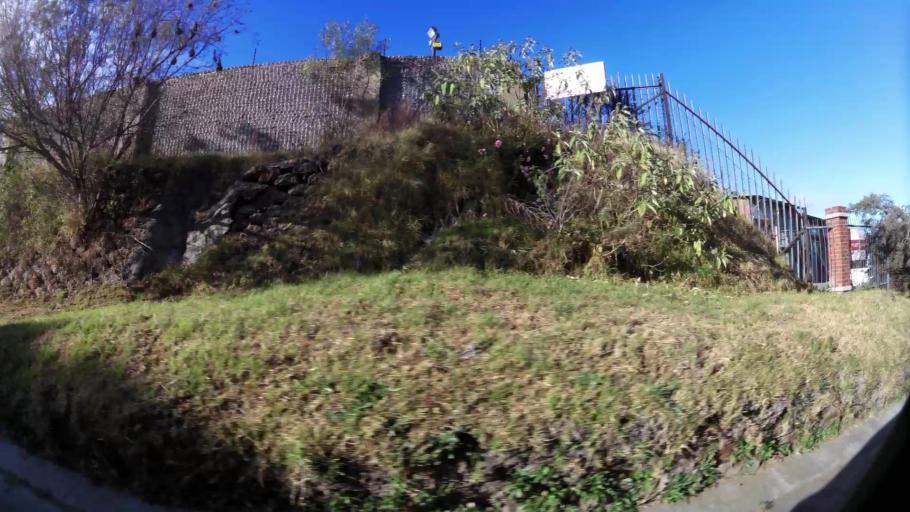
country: ZA
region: Gauteng
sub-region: City of Johannesburg Metropolitan Municipality
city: Midrand
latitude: -26.0334
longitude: 28.1539
